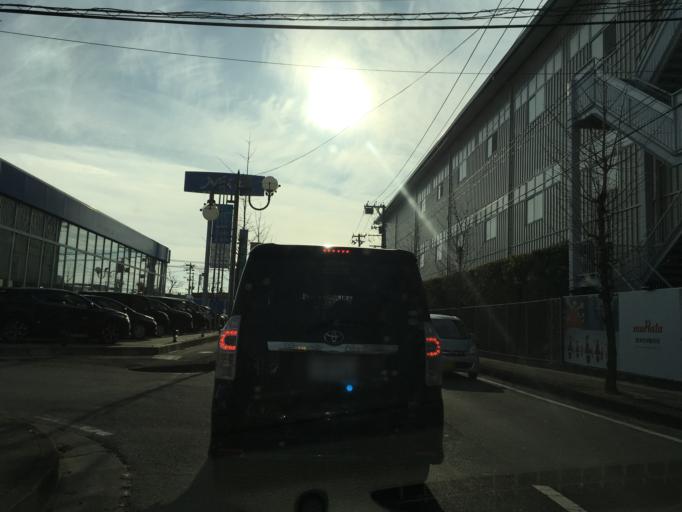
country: JP
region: Miyagi
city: Wakuya
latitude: 38.6882
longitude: 141.1882
